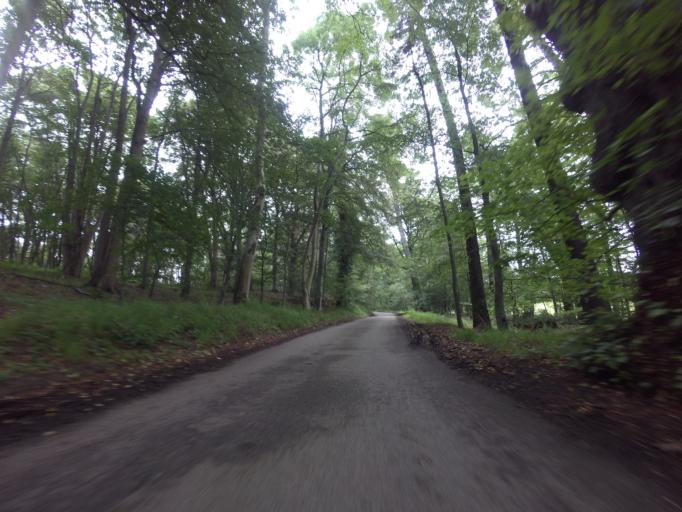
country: GB
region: Scotland
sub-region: Moray
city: Lhanbryd
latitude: 57.6543
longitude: -3.2325
